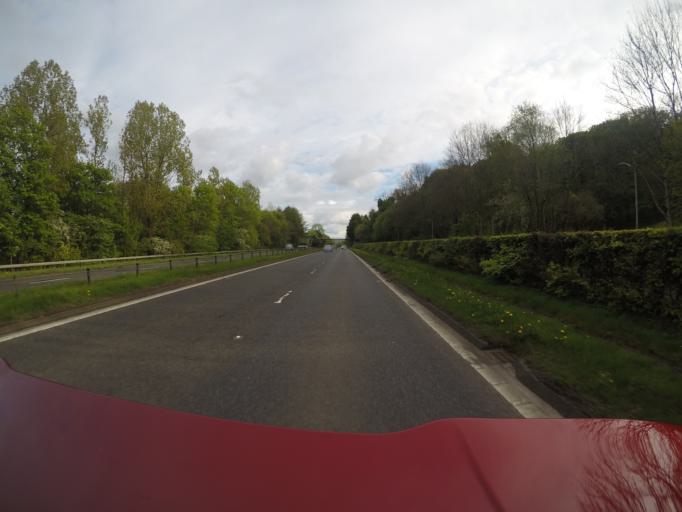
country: GB
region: Scotland
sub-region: West Dunbartonshire
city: Renton
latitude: 55.9710
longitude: -4.5877
